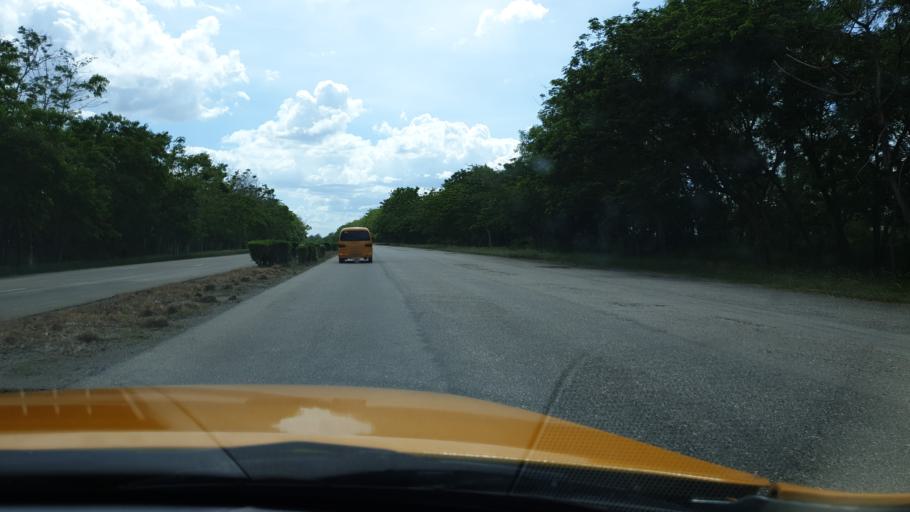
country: CU
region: Cienfuegos
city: Cruces
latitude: 22.4552
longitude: -80.3064
